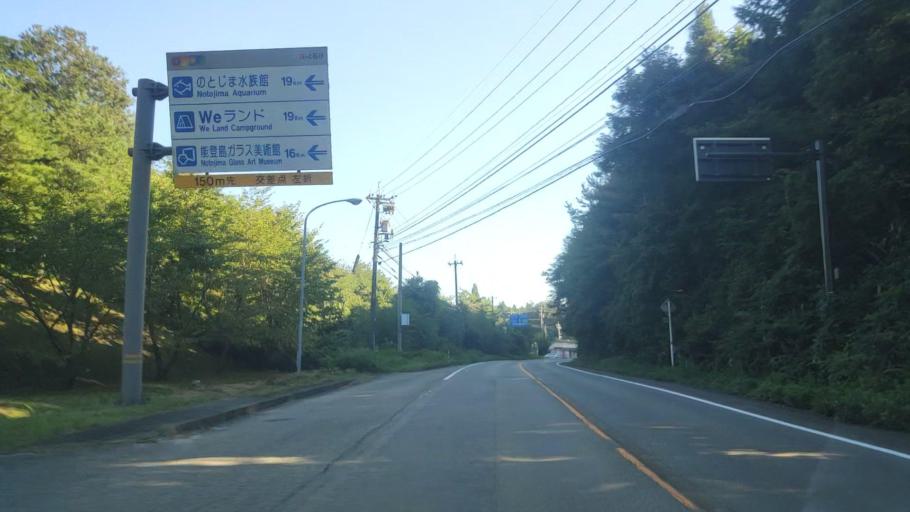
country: JP
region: Ishikawa
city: Nanao
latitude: 37.1331
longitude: 136.8633
